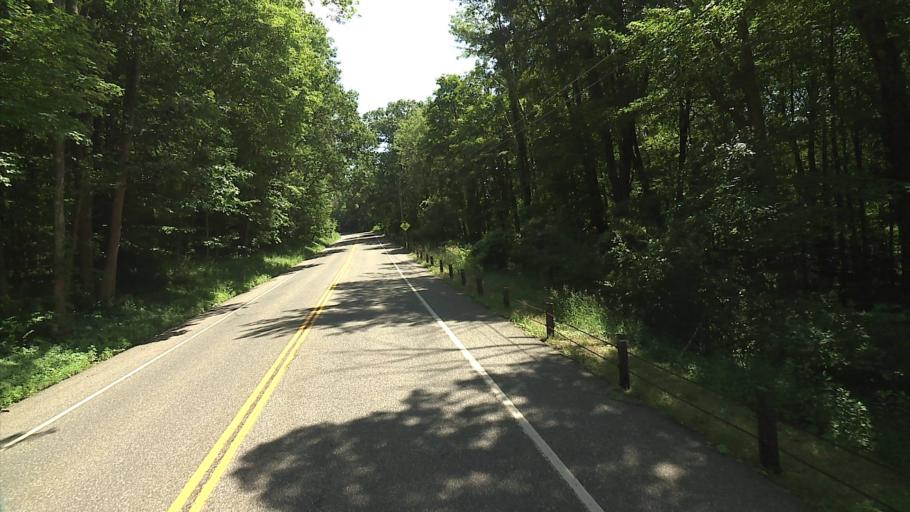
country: US
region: Connecticut
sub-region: Litchfield County
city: Canaan
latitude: 41.8596
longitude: -73.3265
